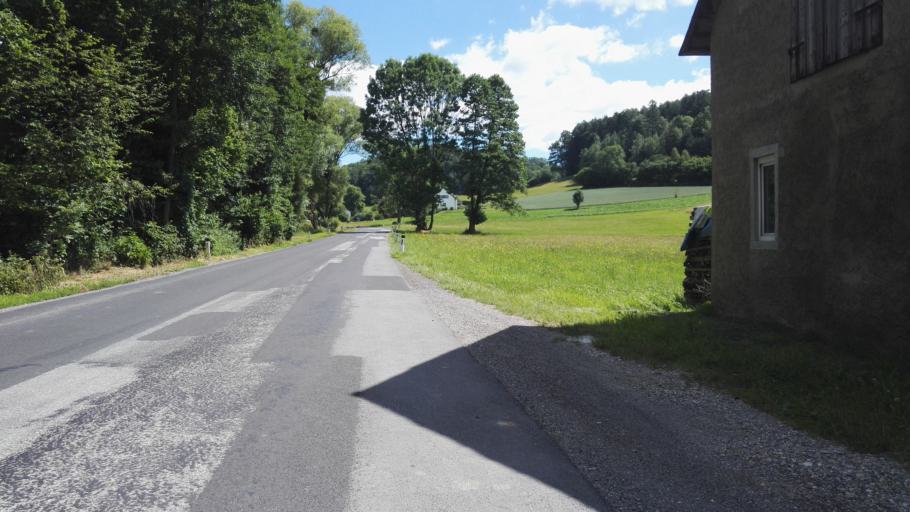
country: AT
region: Styria
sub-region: Politischer Bezirk Graz-Umgebung
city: Eggersdorf bei Graz
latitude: 47.0908
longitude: 15.5454
